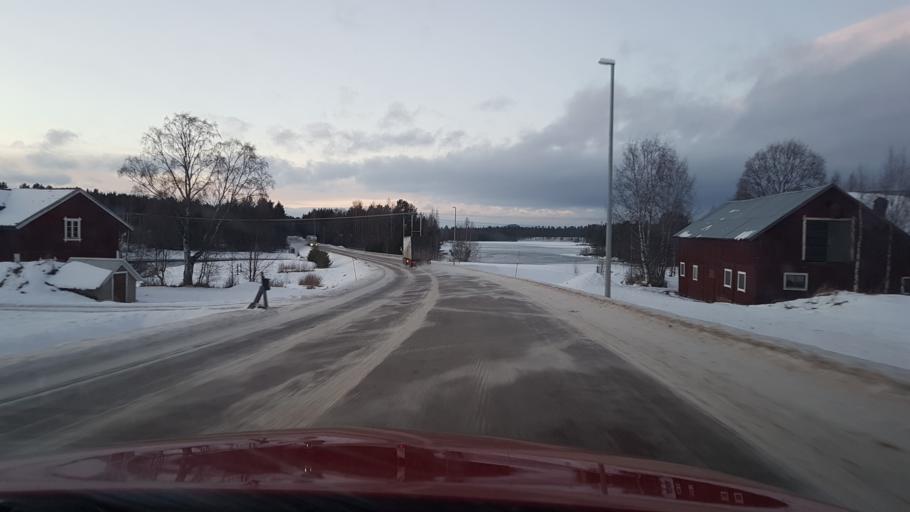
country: SE
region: Jaemtland
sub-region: Harjedalens Kommun
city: Sveg
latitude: 62.0232
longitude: 14.4575
